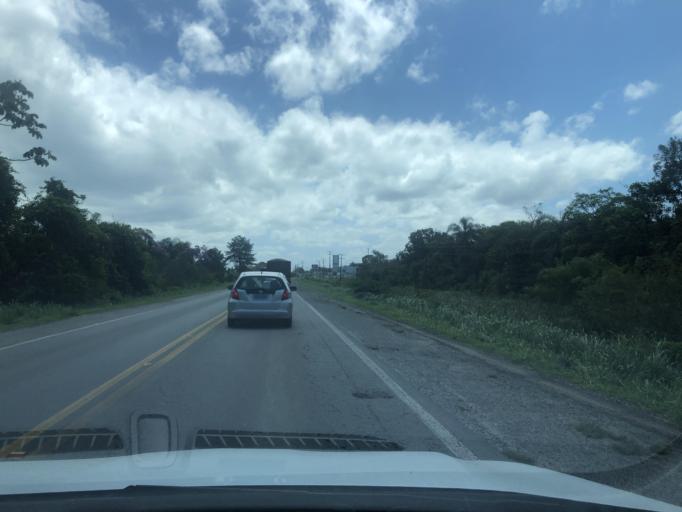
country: BR
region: Santa Catarina
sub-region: Sao Francisco Do Sul
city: Sao Francisco do Sul
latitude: -26.3709
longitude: -48.7018
